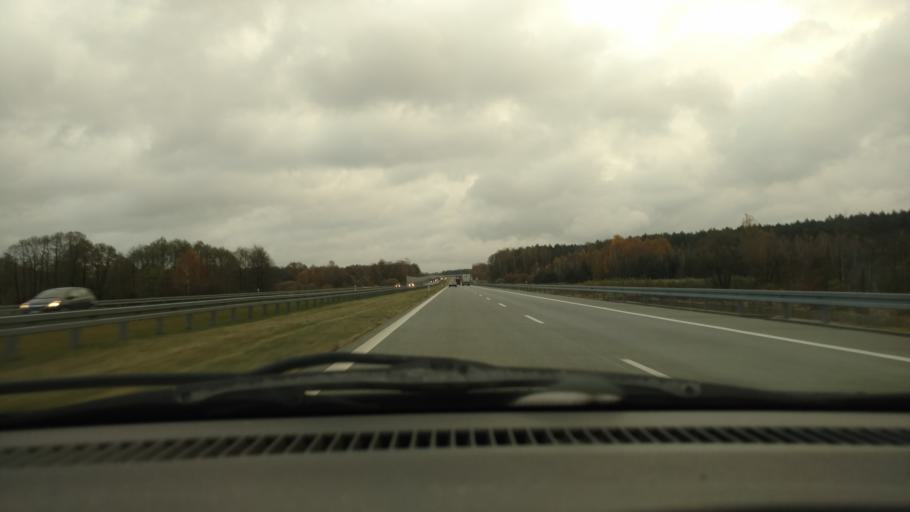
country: PL
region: Lodz Voivodeship
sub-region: Powiat pabianicki
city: Ksawerow
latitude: 51.6311
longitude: 19.4176
